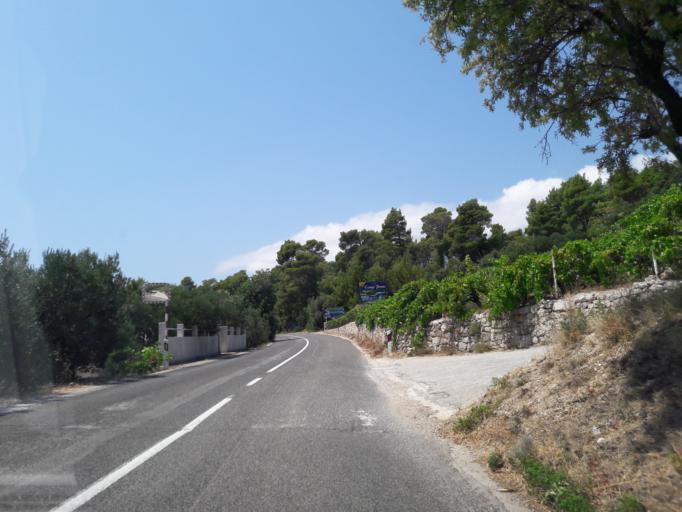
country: HR
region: Dubrovacko-Neretvanska
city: Orebic
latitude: 42.9790
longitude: 17.2252
